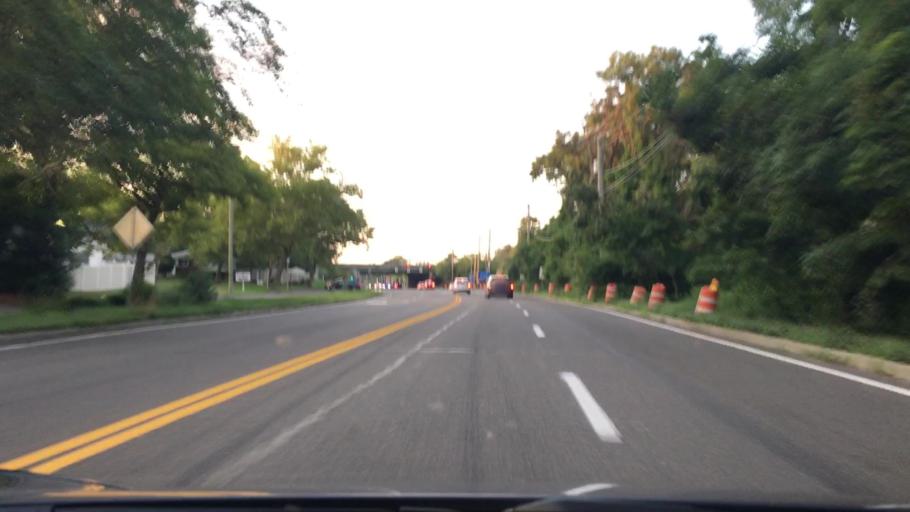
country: US
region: New York
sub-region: Suffolk County
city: Commack
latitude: 40.8024
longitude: -73.2951
